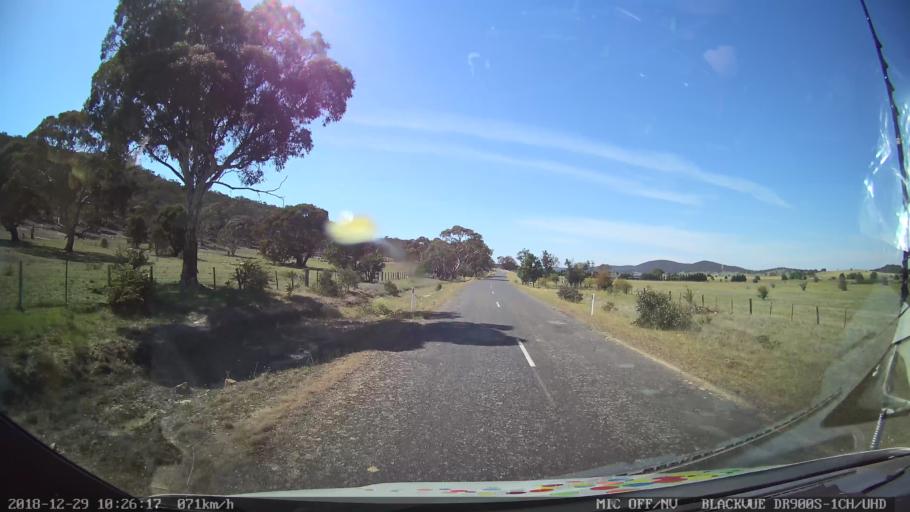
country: AU
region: New South Wales
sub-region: Yass Valley
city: Gundaroo
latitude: -34.9243
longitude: 149.4425
